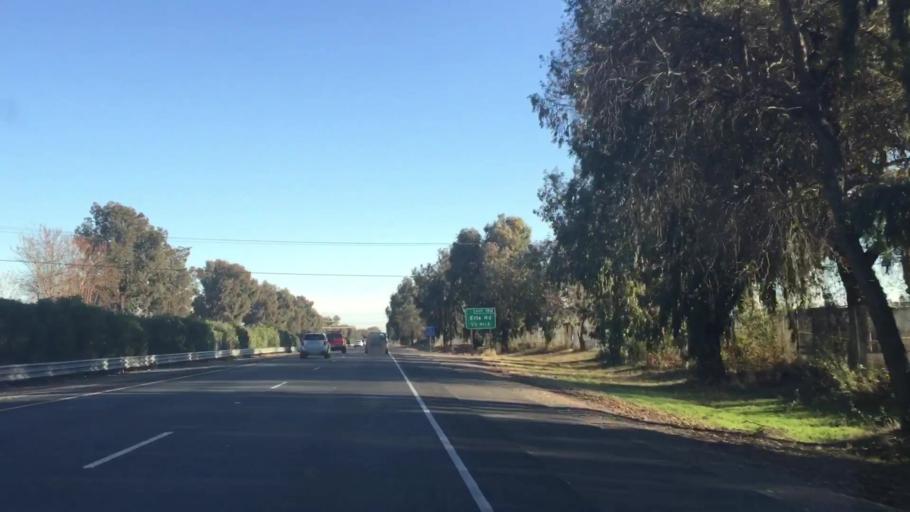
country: US
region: California
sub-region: Yuba County
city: Linda
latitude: 39.1201
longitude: -121.5701
